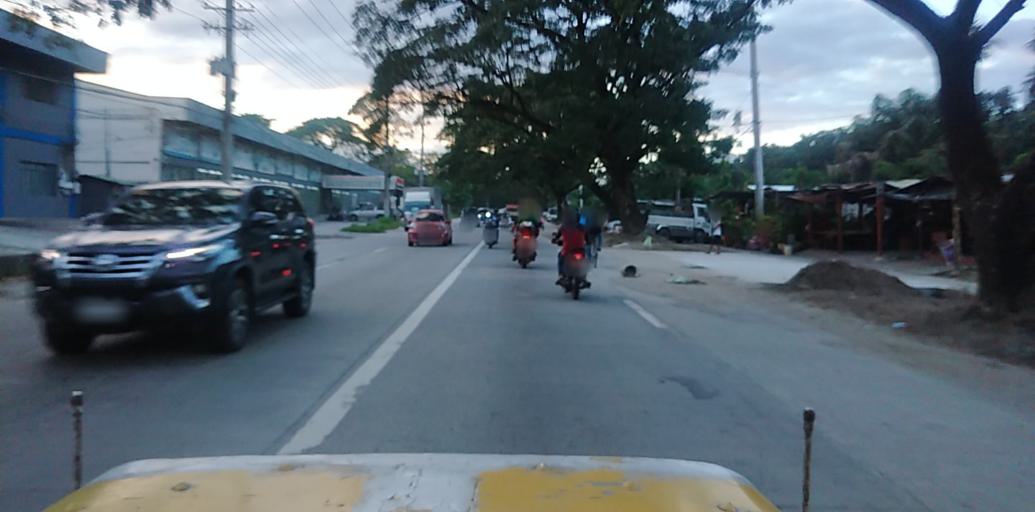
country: PH
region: Central Luzon
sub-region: Province of Pampanga
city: Calibutbut
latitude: 15.1264
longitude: 120.5816
